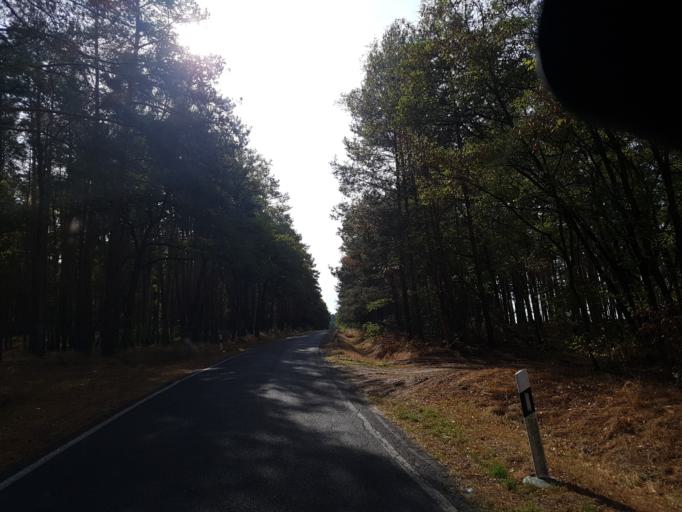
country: DE
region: Brandenburg
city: Schlieben
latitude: 51.7908
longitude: 13.3195
